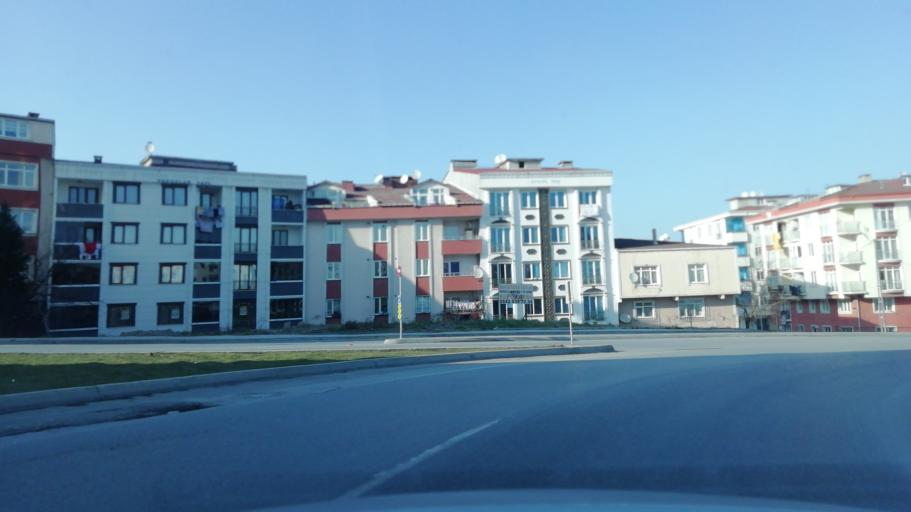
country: TR
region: Istanbul
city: Esenyurt
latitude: 41.0382
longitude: 28.6880
